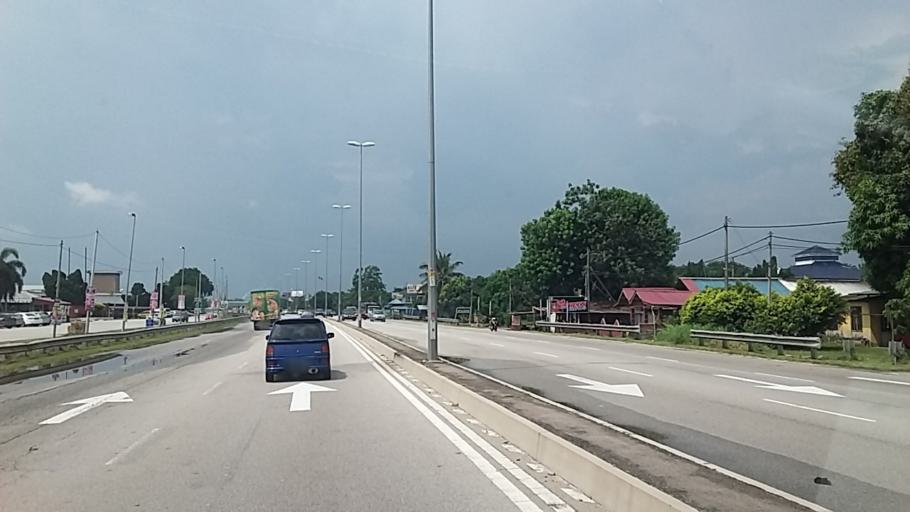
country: MY
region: Johor
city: Parit Raja
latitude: 1.8541
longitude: 103.0919
